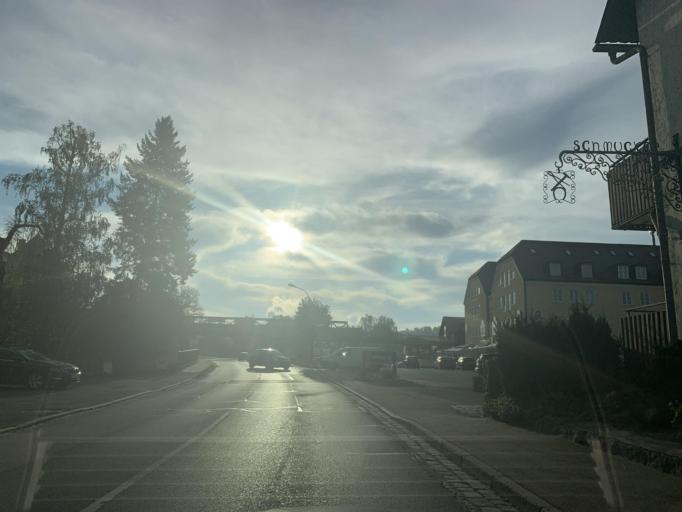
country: DE
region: Bavaria
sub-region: Upper Palatinate
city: Neunburg vorm Wald
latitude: 49.3484
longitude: 12.3827
